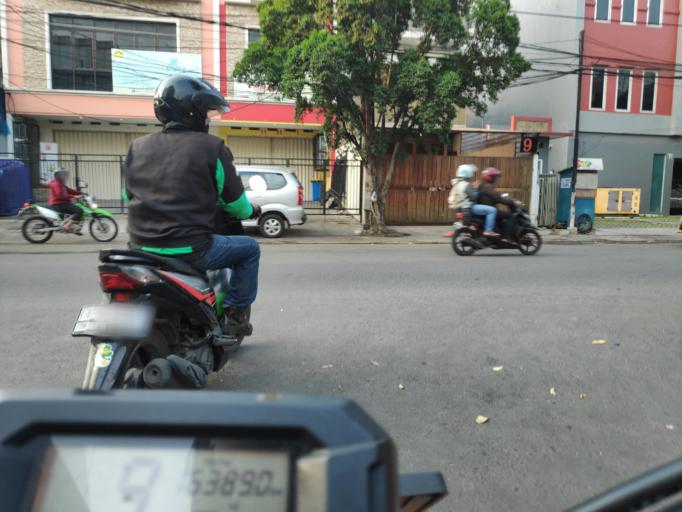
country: ID
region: Jakarta Raya
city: Jakarta
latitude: -6.2561
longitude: 106.7945
